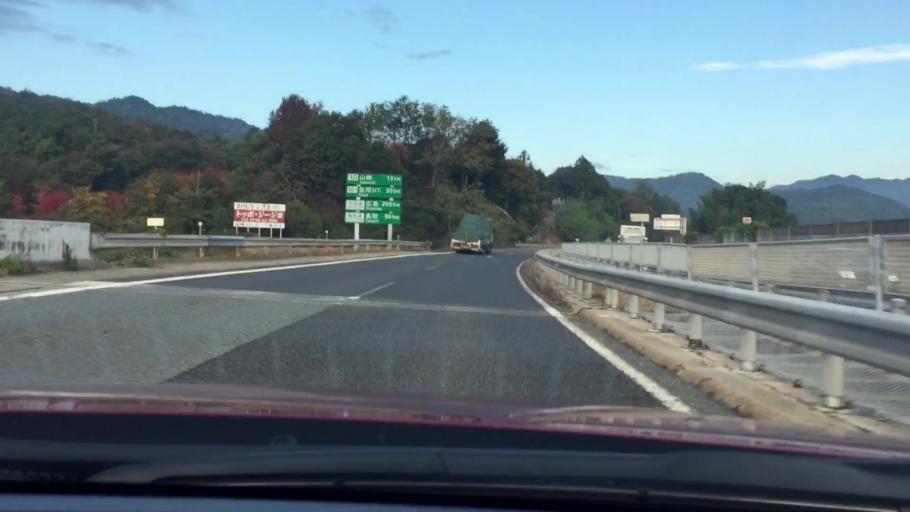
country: JP
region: Hyogo
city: Yamazakicho-nakabirose
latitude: 34.9639
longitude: 134.6803
